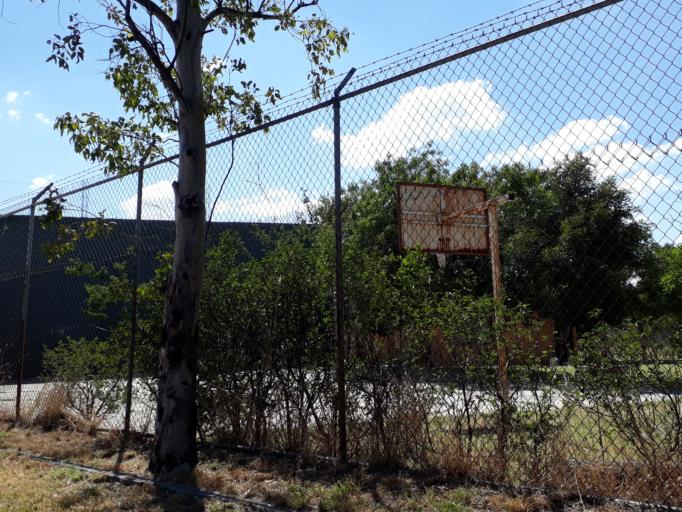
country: MX
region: Aguascalientes
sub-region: Aguascalientes
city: San Sebastian [Fraccionamiento]
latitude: 21.7911
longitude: -102.2759
